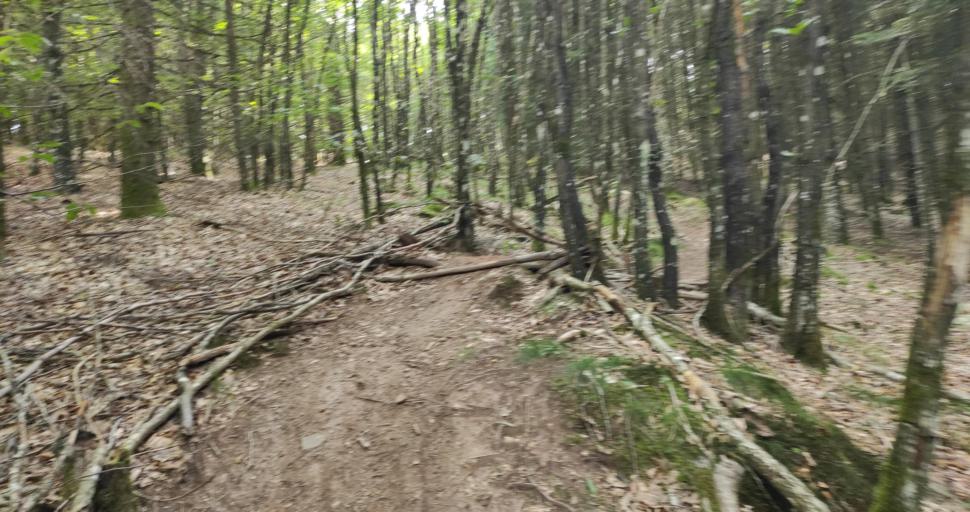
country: FR
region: Midi-Pyrenees
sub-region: Departement de l'Aveyron
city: La Loubiere
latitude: 44.3719
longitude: 2.7244
